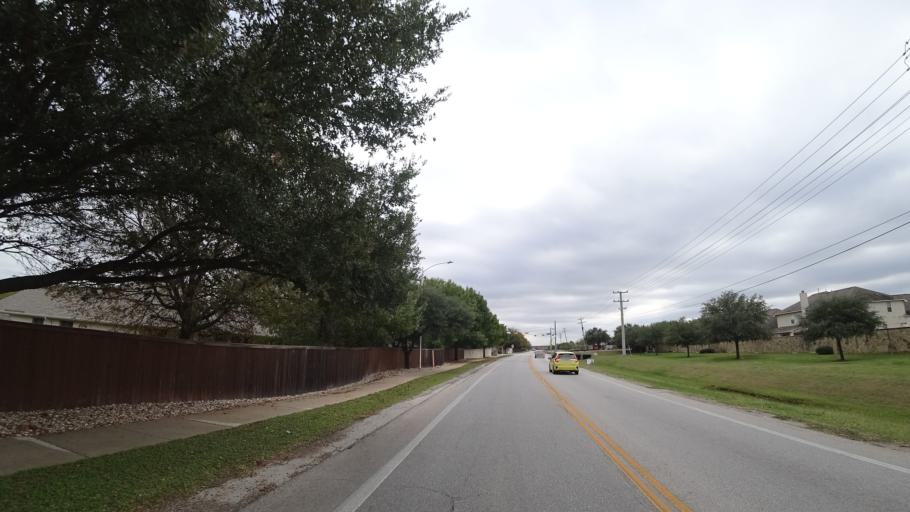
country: US
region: Texas
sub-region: Travis County
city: Shady Hollow
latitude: 30.1536
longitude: -97.8574
